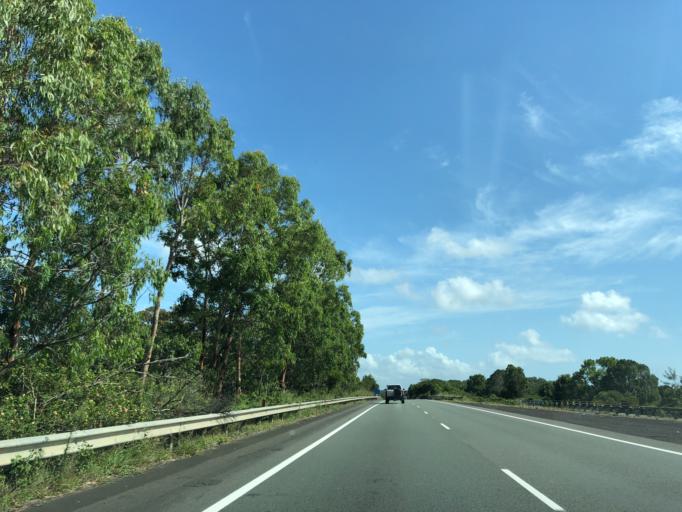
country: AU
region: New South Wales
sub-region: Byron Shire
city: Brunswick Heads
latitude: -28.6057
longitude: 153.5460
